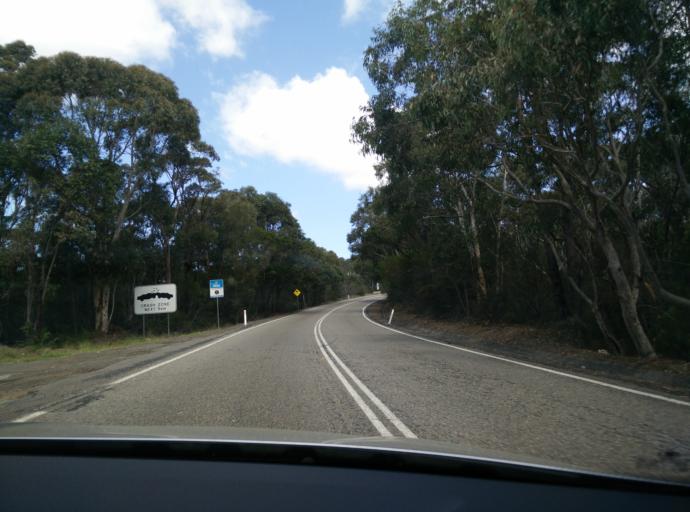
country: AU
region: New South Wales
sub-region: Gosford Shire
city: Point Clare
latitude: -33.4525
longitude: 151.2910
